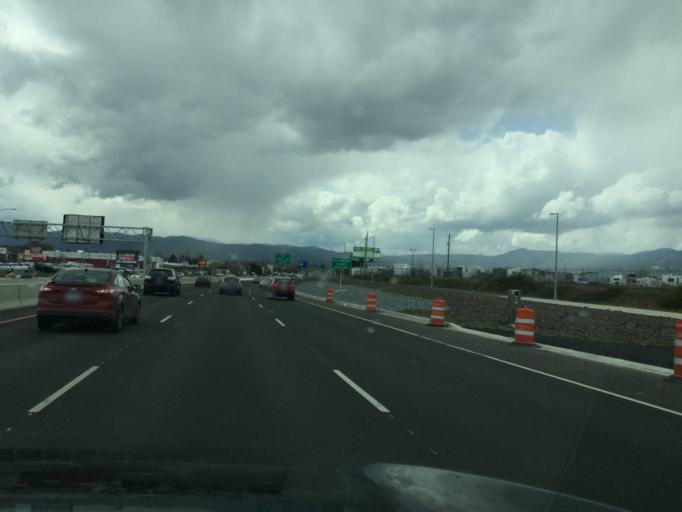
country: US
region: Oregon
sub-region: Jackson County
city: Medford
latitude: 42.3577
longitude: -122.8651
